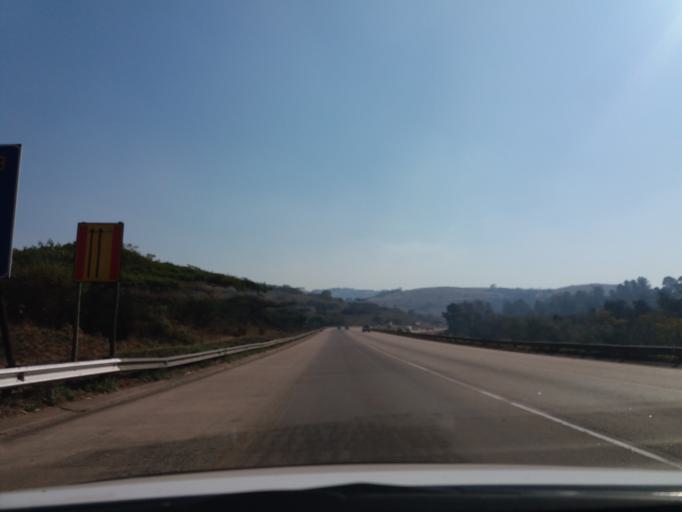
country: ZA
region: KwaZulu-Natal
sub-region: eThekwini Metropolitan Municipality
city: Mpumalanga
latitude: -29.7631
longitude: 30.6767
